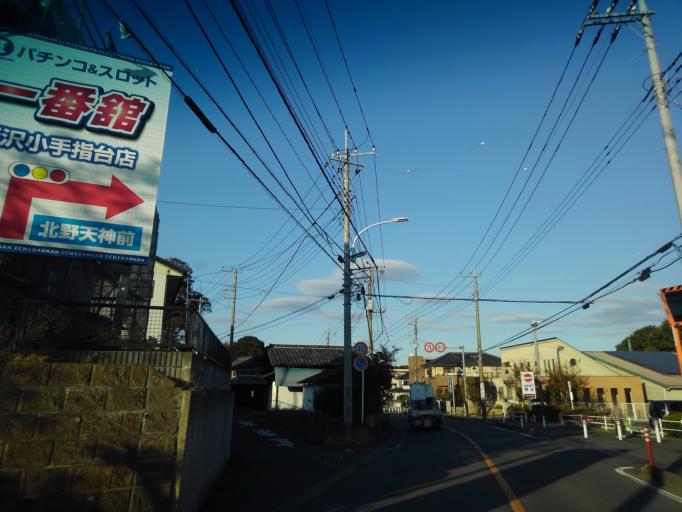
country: JP
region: Saitama
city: Tokorozawa
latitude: 35.7867
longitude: 139.4272
